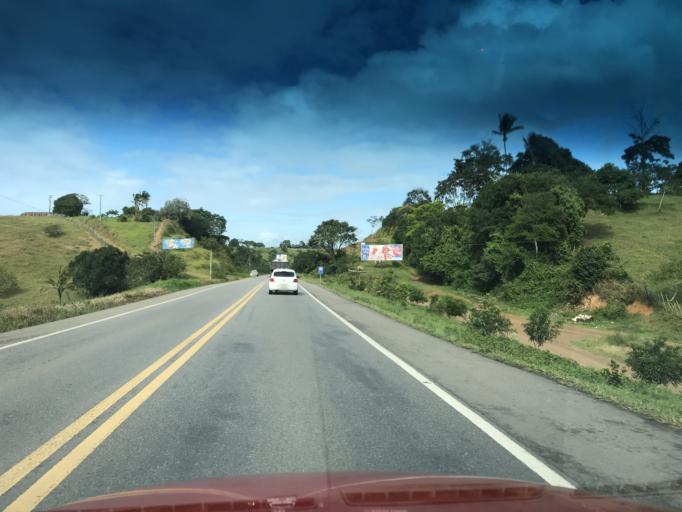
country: BR
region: Bahia
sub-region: Conceicao Do Almeida
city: Muritiba
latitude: -12.9034
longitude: -39.2373
